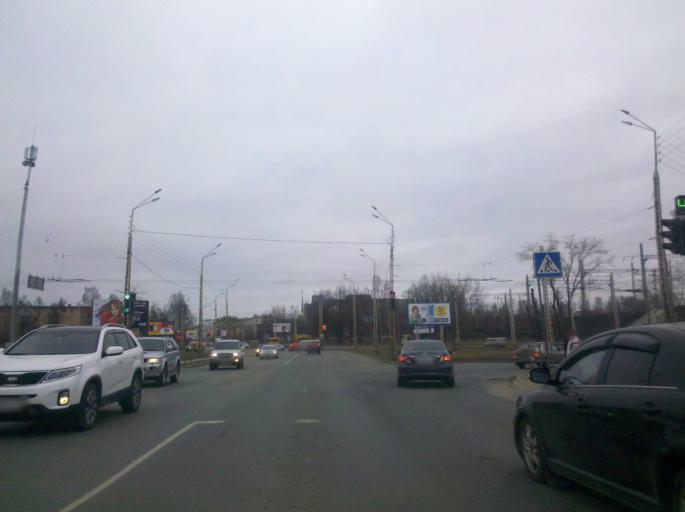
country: RU
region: Republic of Karelia
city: Petrozavodsk
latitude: 61.7896
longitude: 34.3411
